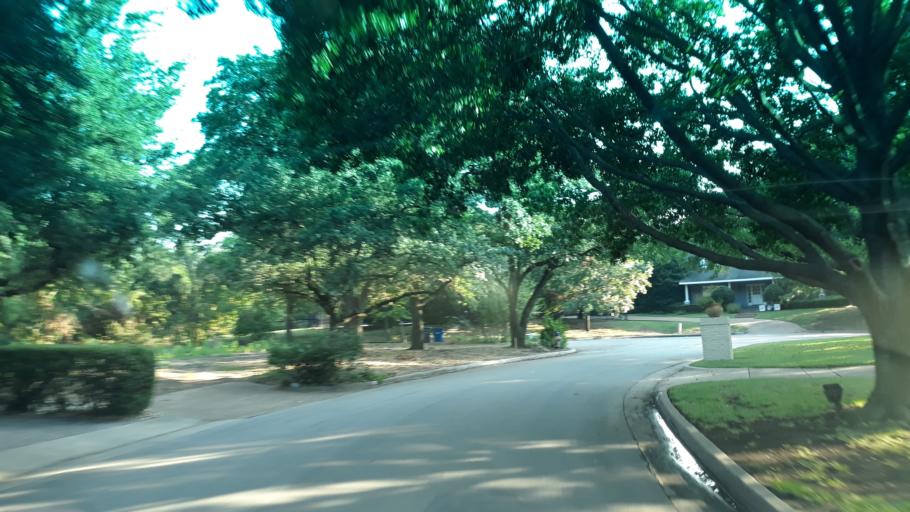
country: US
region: Texas
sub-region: Dallas County
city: Addison
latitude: 32.9430
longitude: -96.7944
